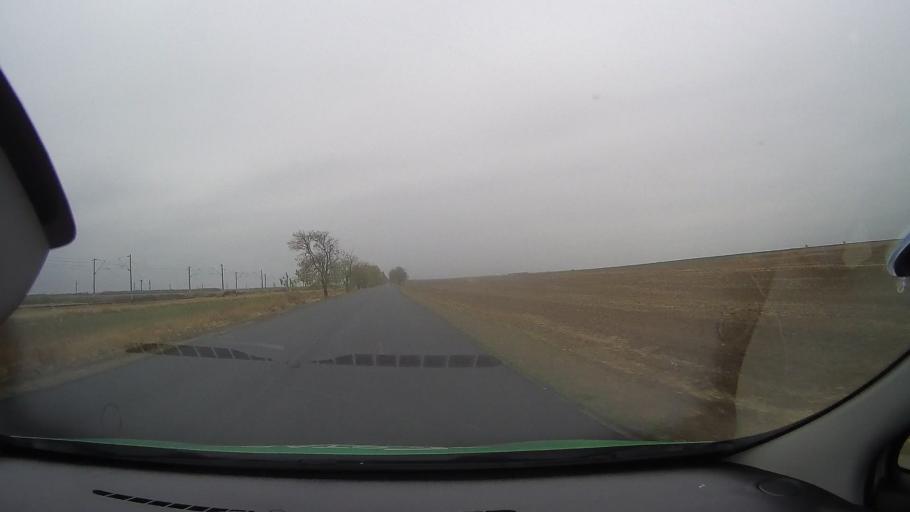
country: RO
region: Ialomita
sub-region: Comuna Valea Ciorii
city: Valea Ciorii
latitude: 44.7013
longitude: 27.5972
